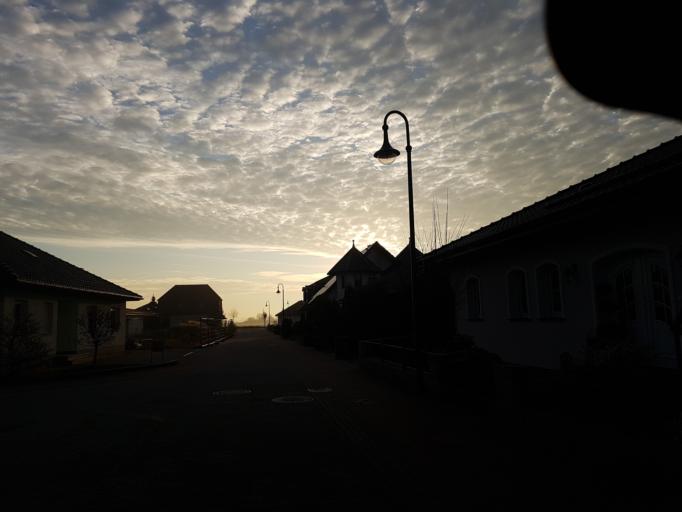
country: DE
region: Saxony-Anhalt
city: Elster
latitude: 51.8336
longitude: 12.8293
